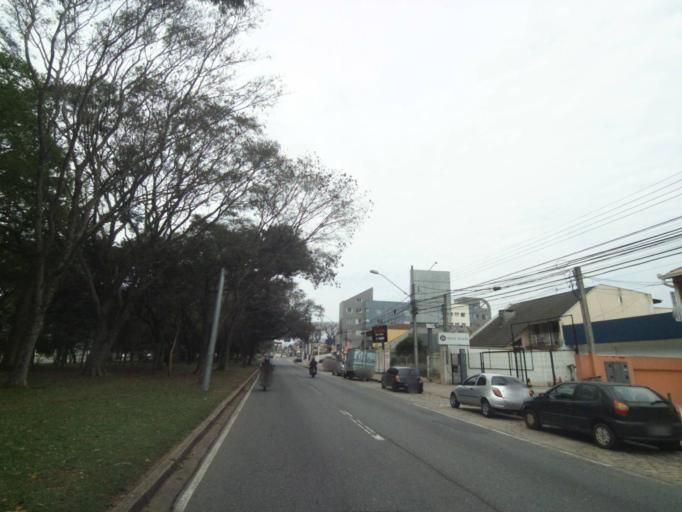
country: BR
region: Parana
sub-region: Curitiba
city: Curitiba
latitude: -25.4554
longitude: -49.3038
